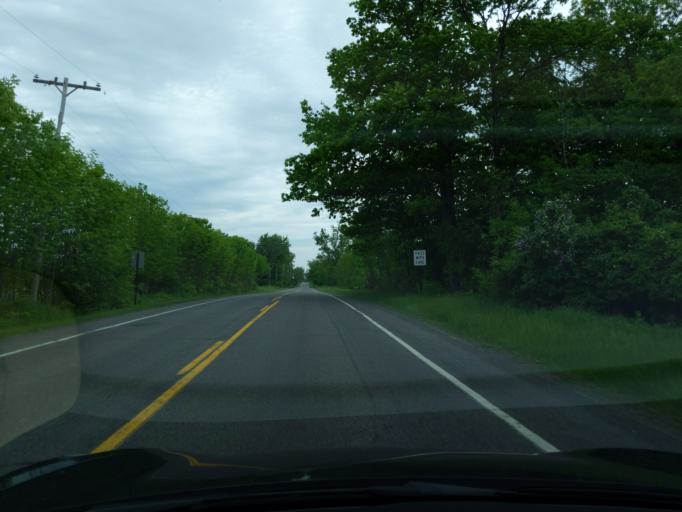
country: US
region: Michigan
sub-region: Ingham County
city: Mason
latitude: 42.5774
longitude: -84.3571
